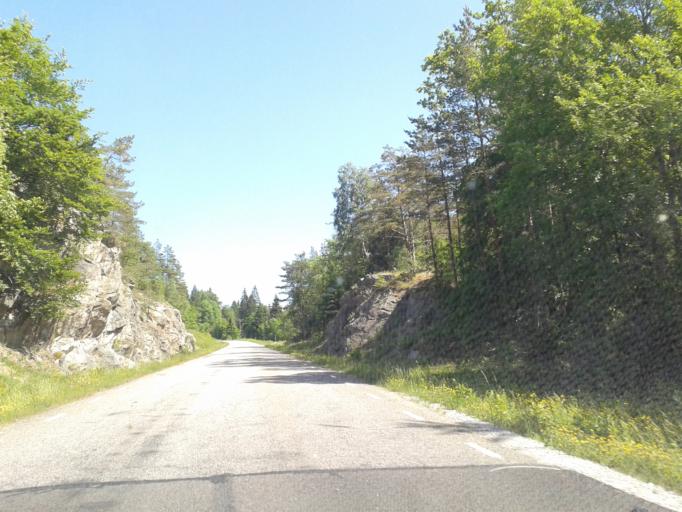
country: SE
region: Vaestra Goetaland
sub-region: Kungalvs Kommun
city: Diserod
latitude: 57.9758
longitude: 11.9562
